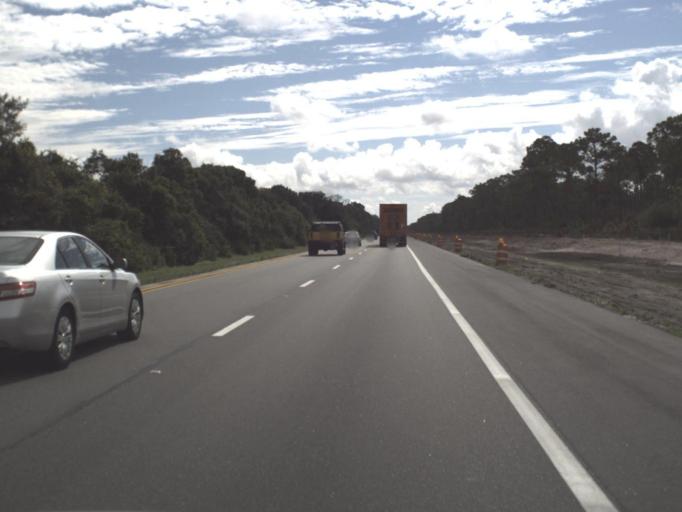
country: US
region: Florida
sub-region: Sarasota County
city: Warm Mineral Springs
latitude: 27.0998
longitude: -82.2674
